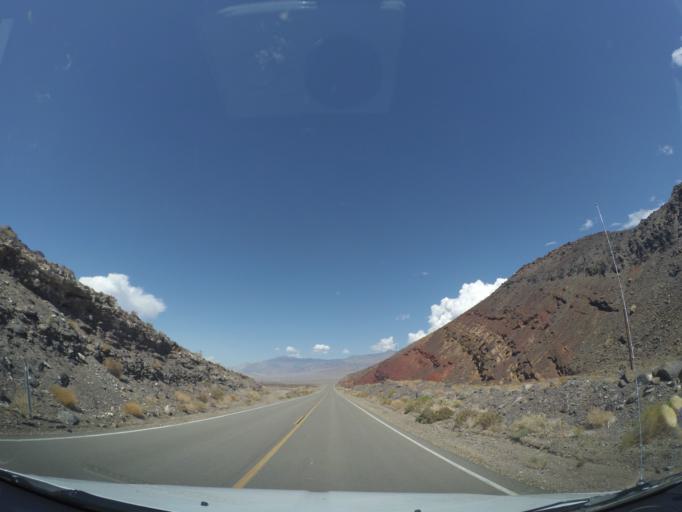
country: US
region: California
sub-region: Inyo County
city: Lone Pine
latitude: 36.3897
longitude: -117.8066
